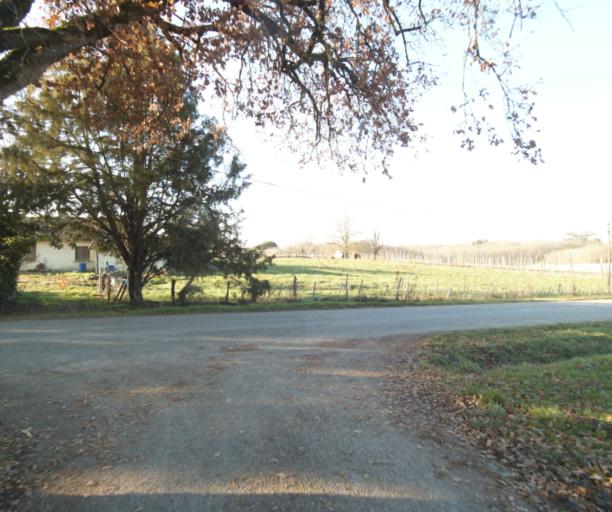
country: FR
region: Midi-Pyrenees
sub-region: Departement du Tarn-et-Garonne
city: Moissac
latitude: 44.1435
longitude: 1.1223
